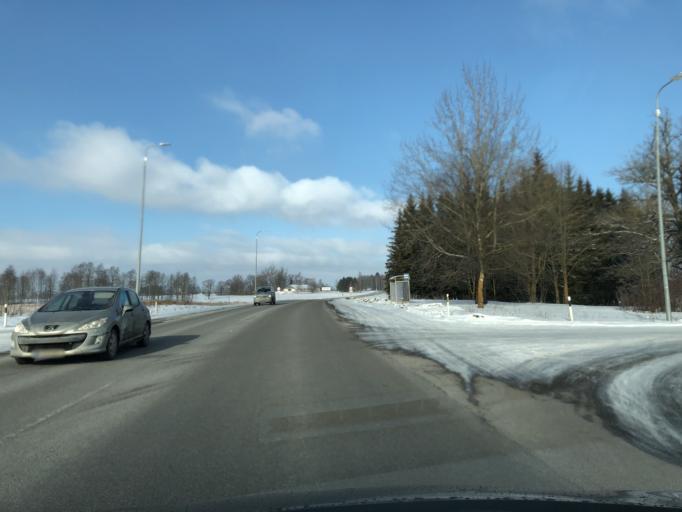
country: EE
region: Jaervamaa
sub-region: Paide linn
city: Paide
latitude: 58.8302
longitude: 25.7436
